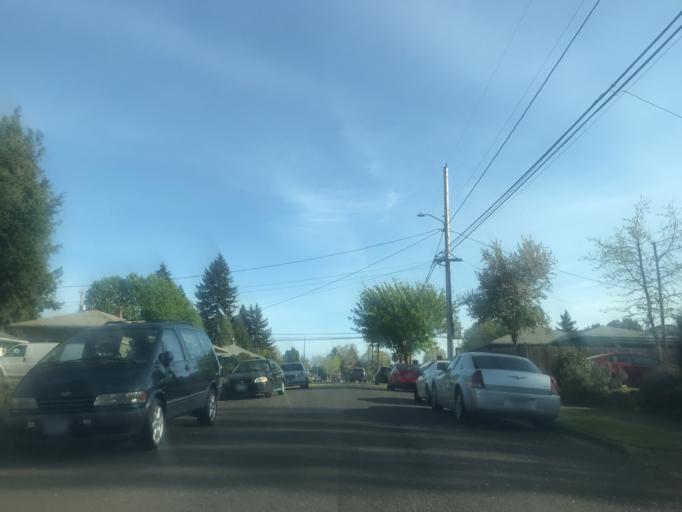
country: US
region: Oregon
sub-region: Multnomah County
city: Lents
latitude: 45.5026
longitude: -122.5819
